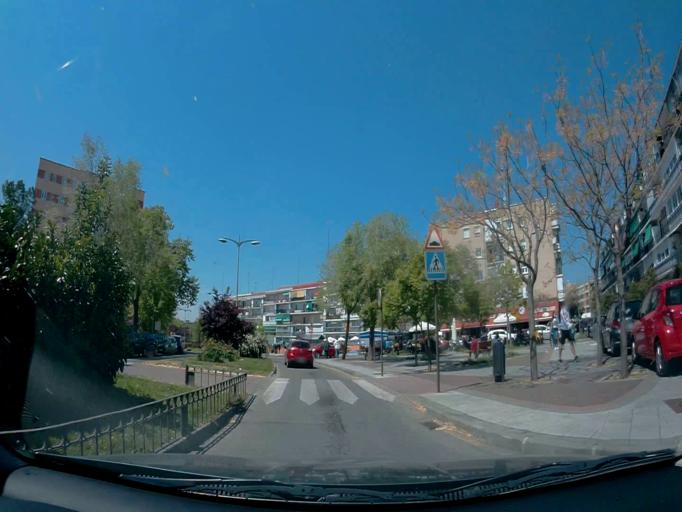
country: ES
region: Madrid
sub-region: Provincia de Madrid
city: Alcorcon
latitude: 40.3422
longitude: -3.8253
